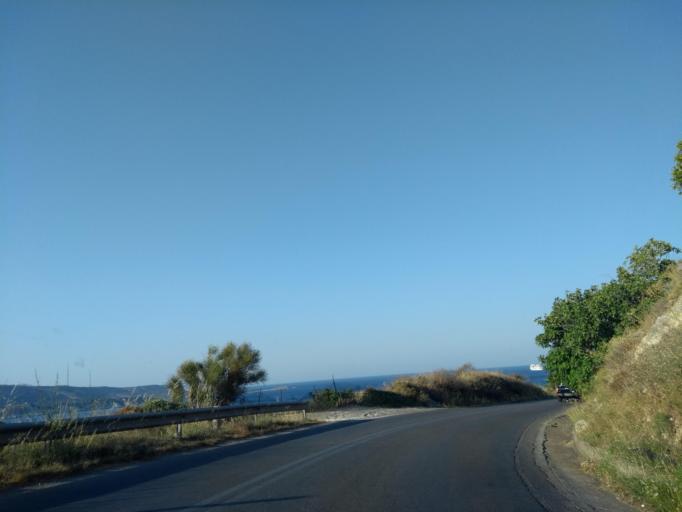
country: GR
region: Crete
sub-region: Nomos Chanias
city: Kalivai
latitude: 35.4704
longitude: 24.1485
